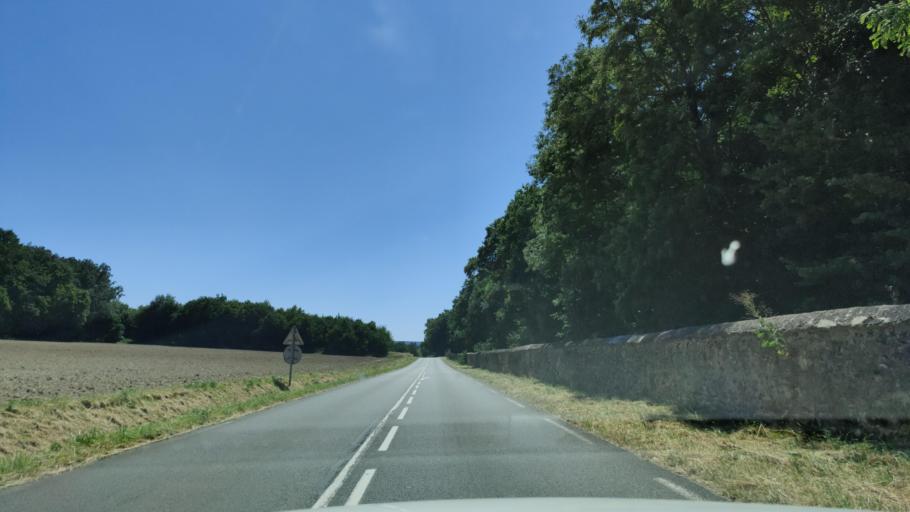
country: FR
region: Ile-de-France
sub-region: Departement de l'Essonne
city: Fontenay-les-Briis
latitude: 48.6053
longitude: 2.1660
